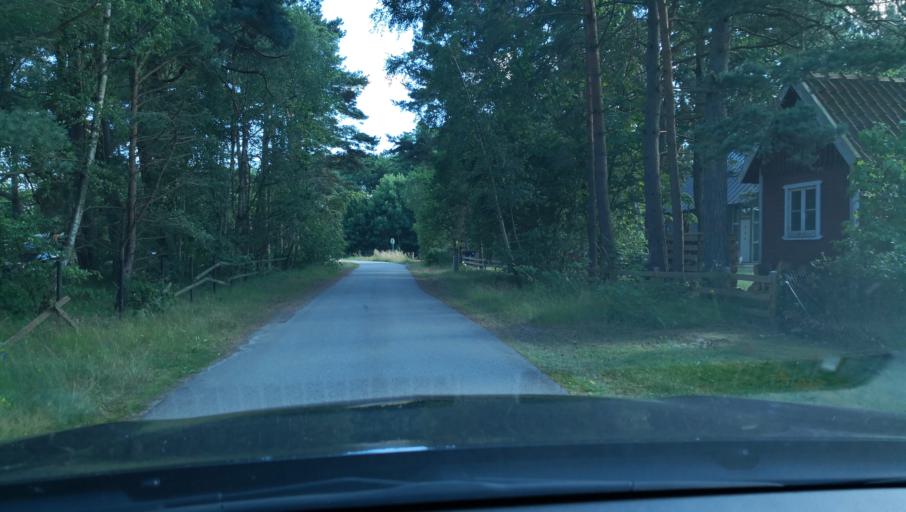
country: SE
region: Skane
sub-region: Simrishamns Kommun
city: Kivik
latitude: 55.7672
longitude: 14.1953
